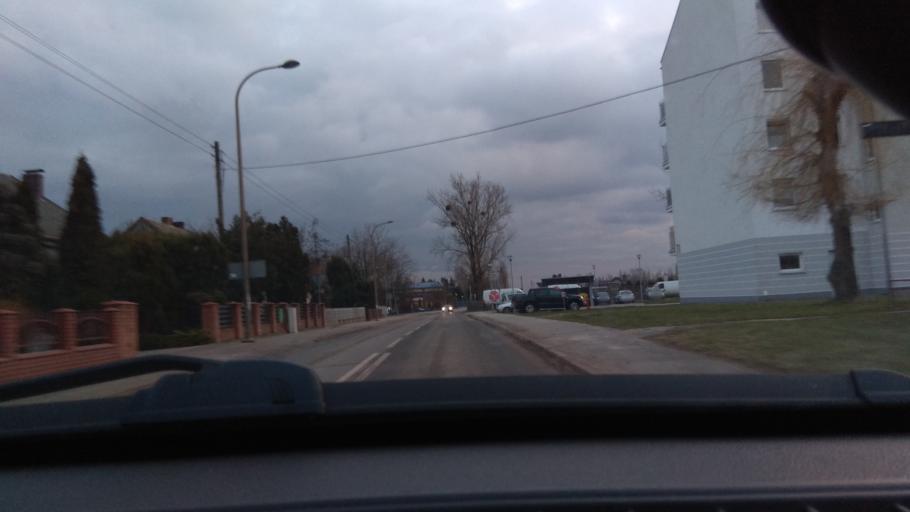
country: PL
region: Greater Poland Voivodeship
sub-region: Powiat kepinski
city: Kepno
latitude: 51.3004
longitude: 18.0056
